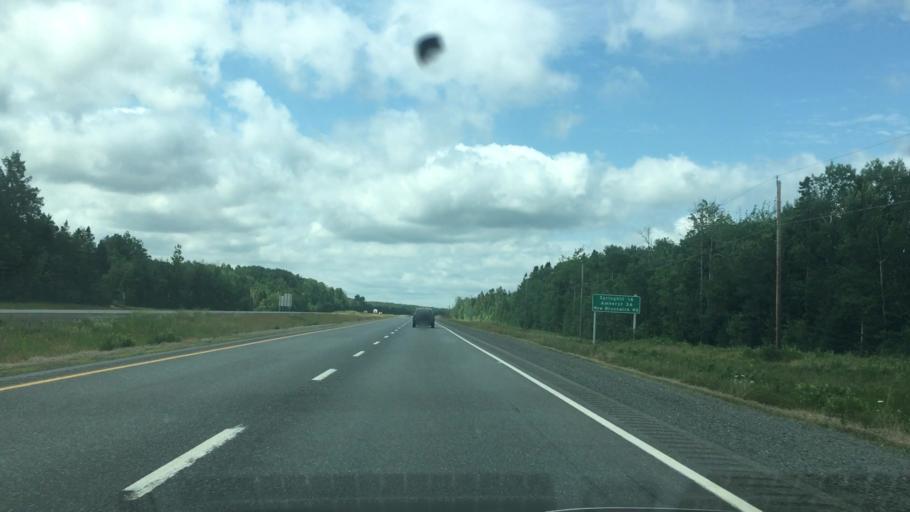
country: CA
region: Nova Scotia
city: Oxford
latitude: 45.7221
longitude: -63.9002
